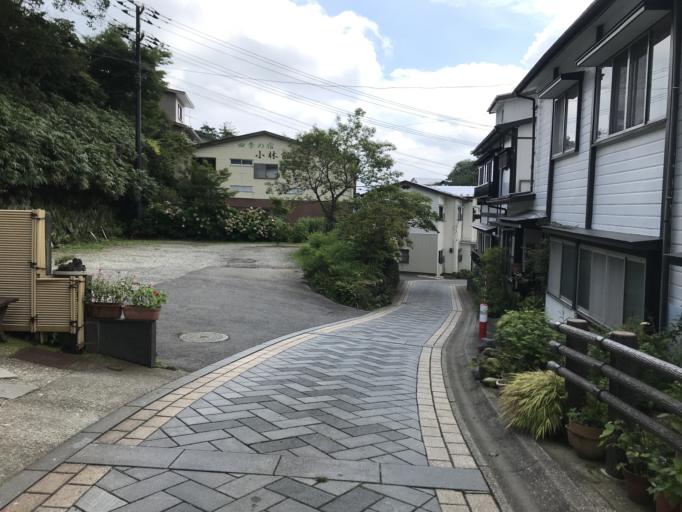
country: JP
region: Tochigi
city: Kuroiso
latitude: 37.0974
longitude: 140.0015
